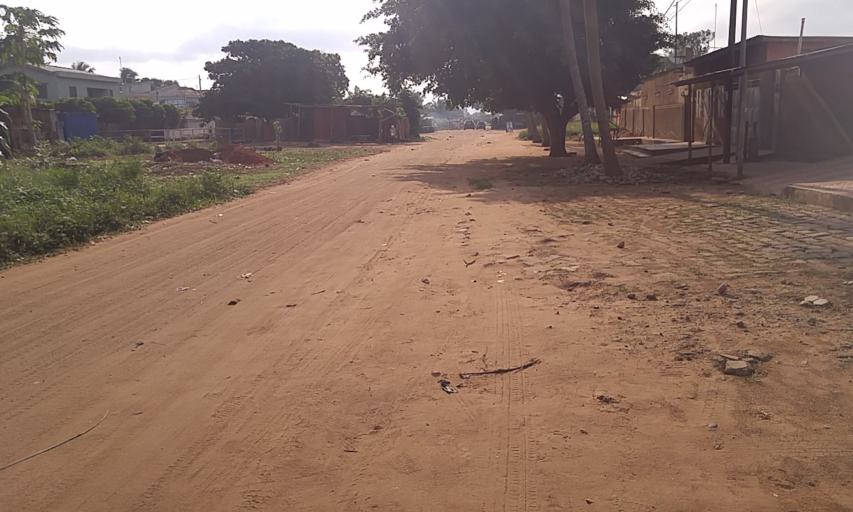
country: TG
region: Maritime
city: Lome
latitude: 6.1794
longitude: 1.1871
